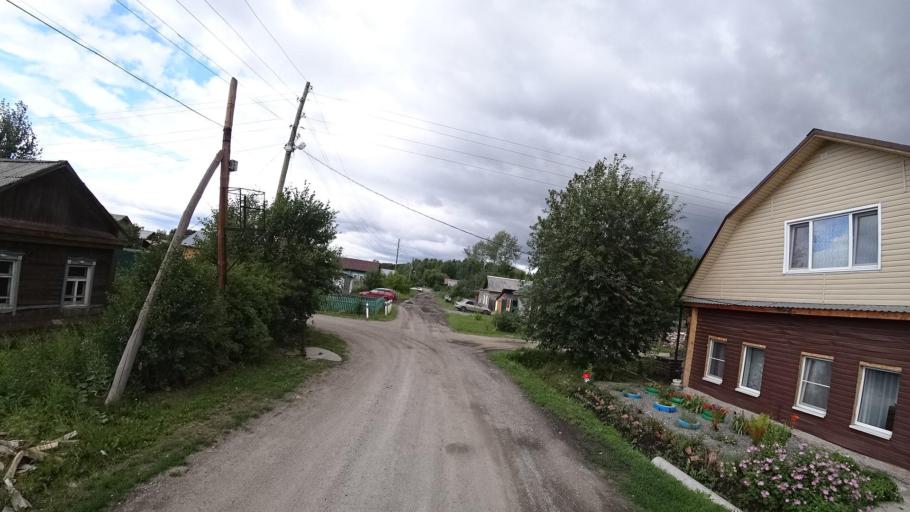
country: RU
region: Sverdlovsk
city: Kamyshlov
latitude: 56.8575
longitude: 62.7185
